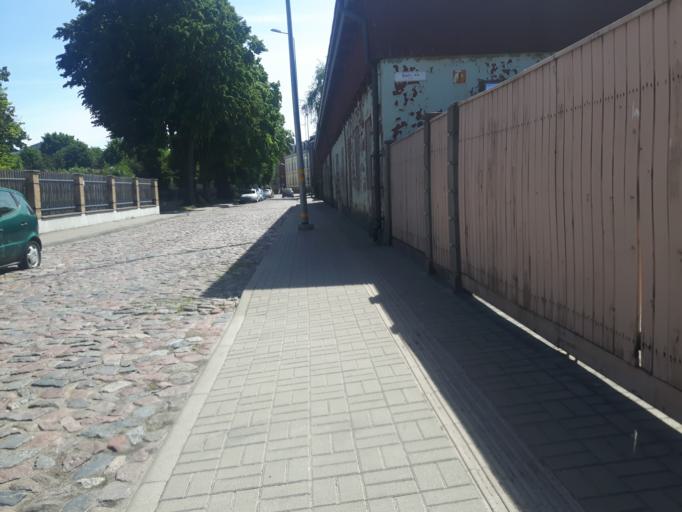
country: LV
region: Liepaja
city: Liepaja
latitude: 56.5115
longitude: 21.0012
